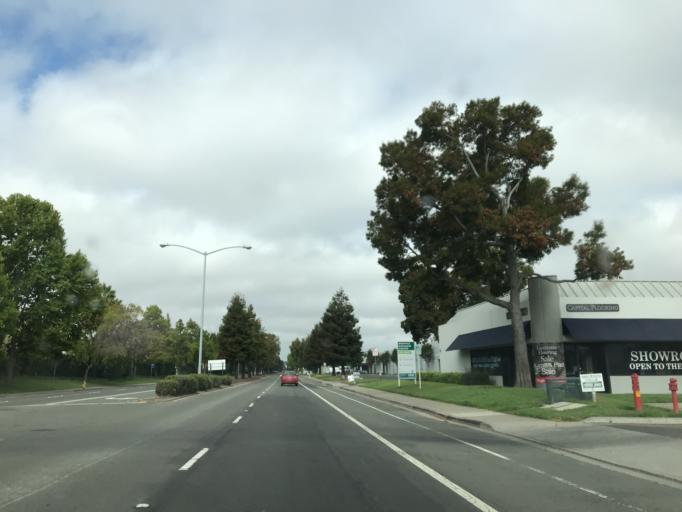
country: US
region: California
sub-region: Alameda County
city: Union City
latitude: 37.6059
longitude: -122.0699
